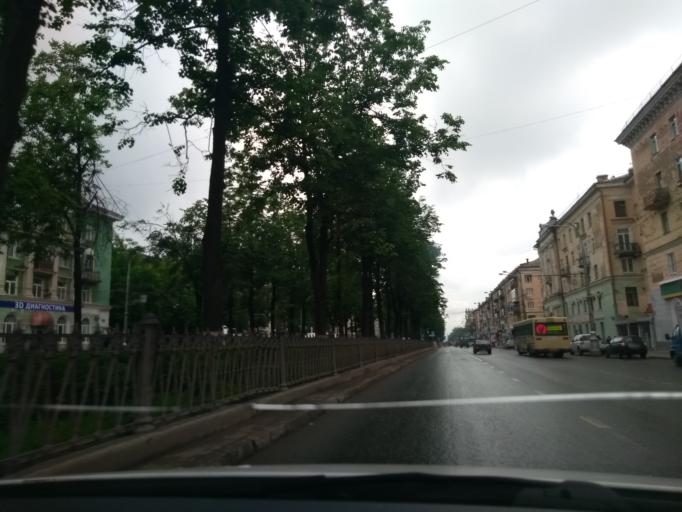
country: RU
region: Perm
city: Perm
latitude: 57.9977
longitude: 56.2519
